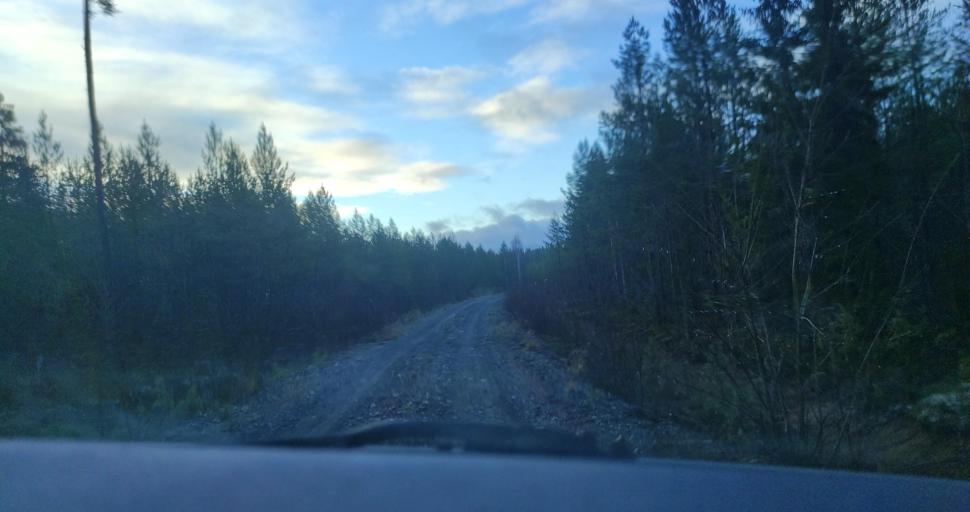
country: RU
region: Republic of Karelia
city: Pitkyaranta
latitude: 61.7393
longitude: 31.3646
